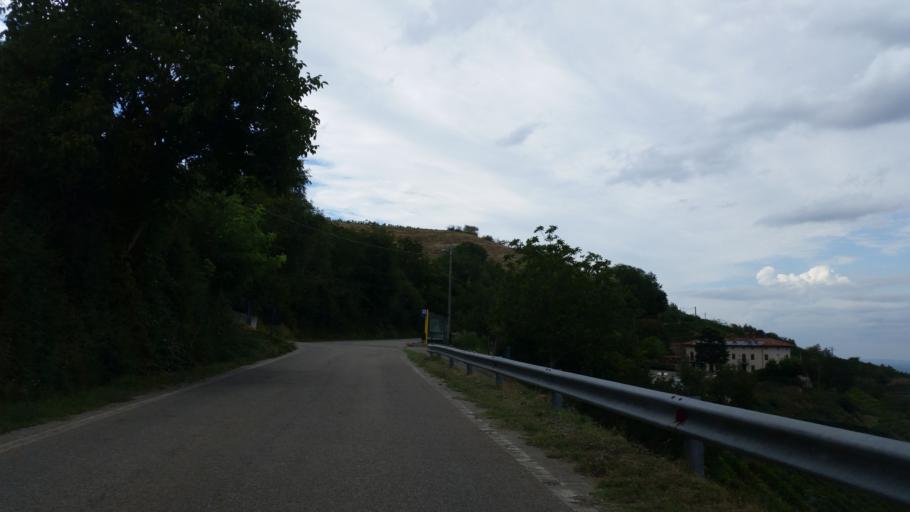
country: IT
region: Piedmont
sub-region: Provincia di Cuneo
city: Neviglie
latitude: 44.6820
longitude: 8.1277
